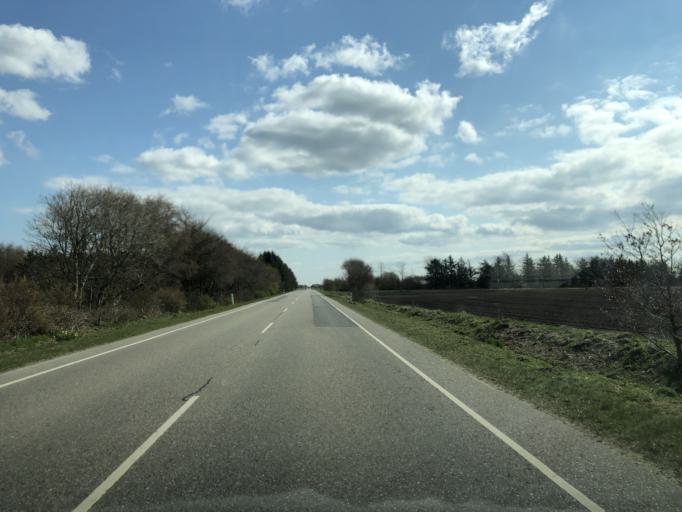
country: DK
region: Central Jutland
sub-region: Lemvig Kommune
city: Lemvig
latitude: 56.4248
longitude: 8.2416
